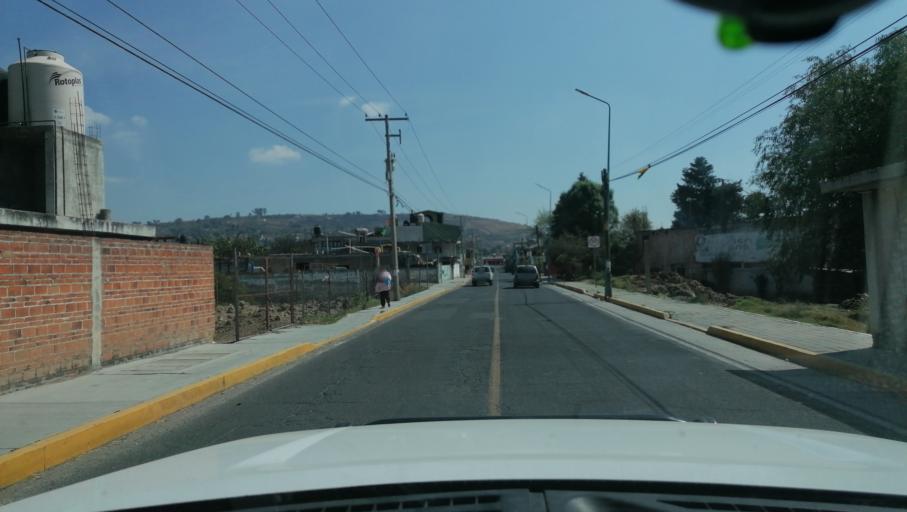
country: MX
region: Tlaxcala
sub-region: San Jeronimo Zacualpan
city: San Jeronimo Zacualpan
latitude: 19.2408
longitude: -98.2660
